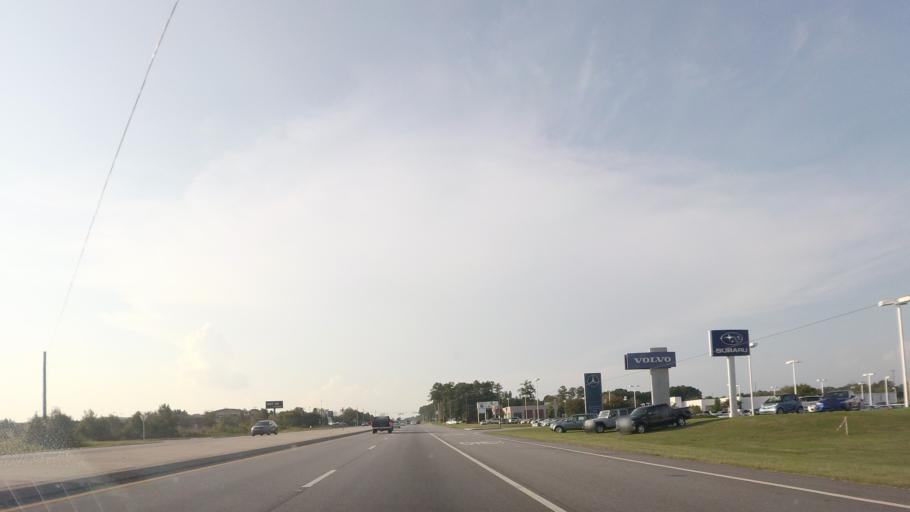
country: US
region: Georgia
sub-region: Bibb County
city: Macon
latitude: 32.9218
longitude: -83.7102
